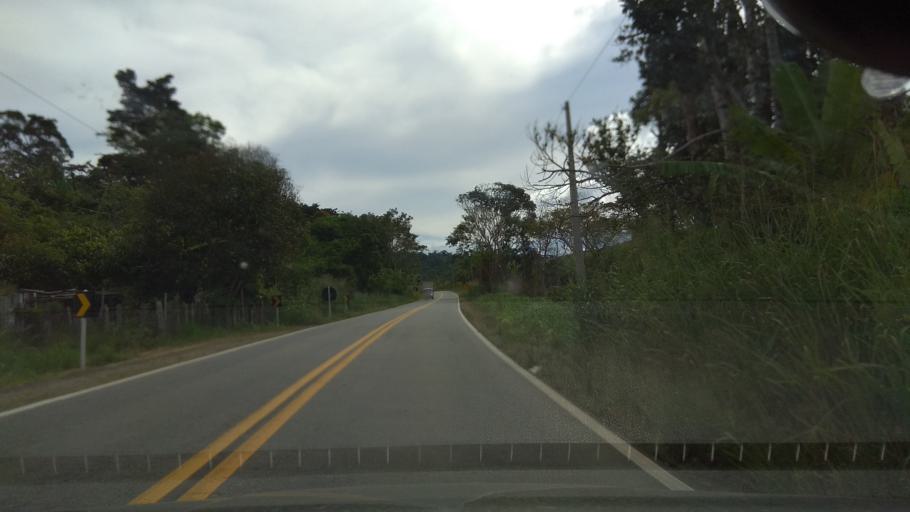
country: BR
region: Bahia
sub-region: Ubata
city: Ubata
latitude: -14.1943
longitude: -39.5564
